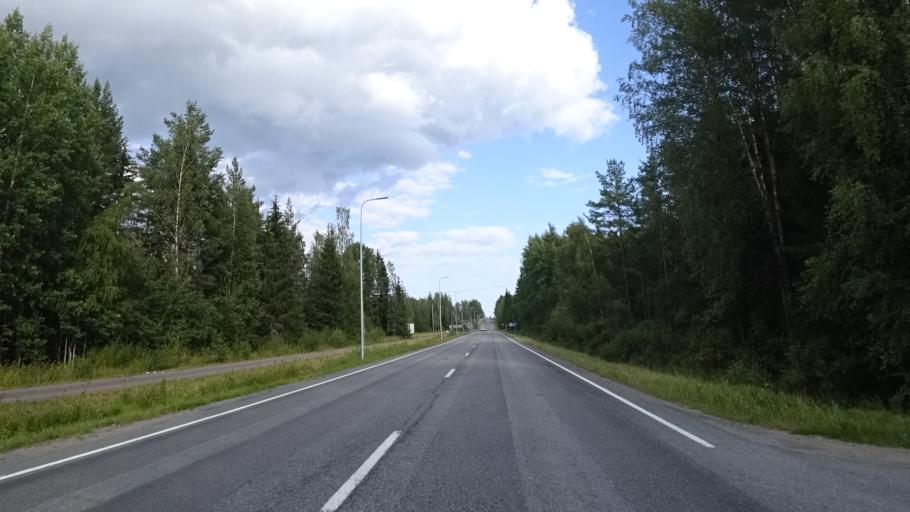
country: FI
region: South Karelia
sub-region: Imatra
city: Imatra
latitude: 61.1732
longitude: 28.7290
